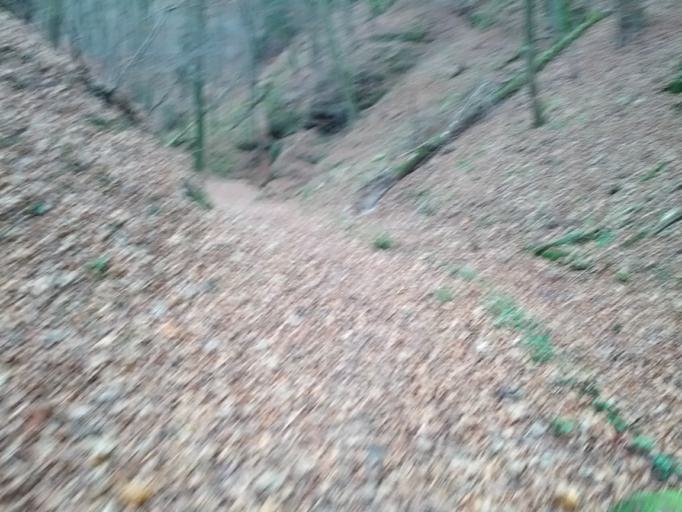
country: DE
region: Thuringia
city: Eisenach
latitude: 50.9498
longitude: 10.3164
